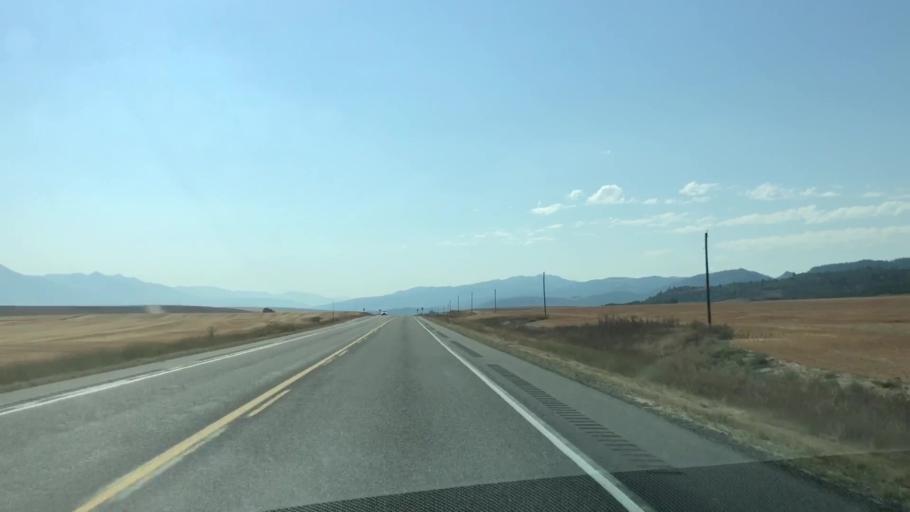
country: US
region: Idaho
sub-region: Teton County
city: Victor
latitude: 43.5052
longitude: -111.4715
